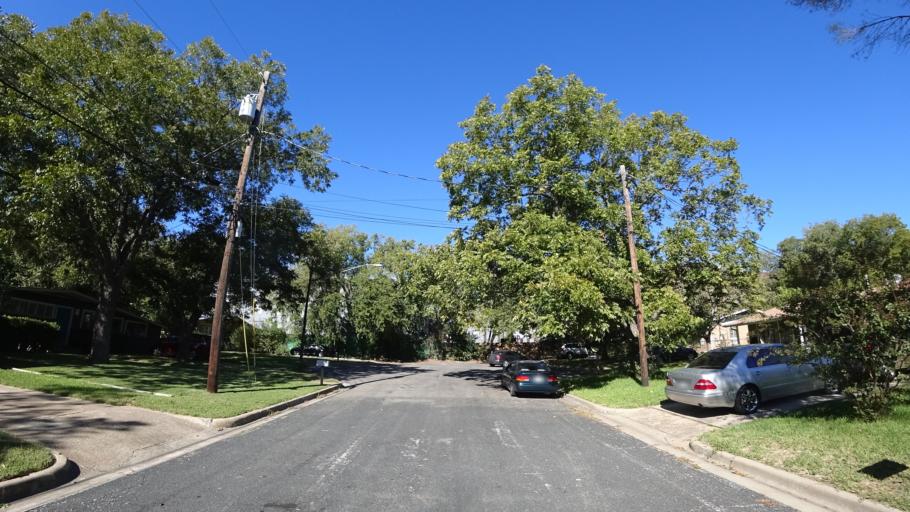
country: US
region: Texas
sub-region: Travis County
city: Austin
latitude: 30.3308
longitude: -97.7204
